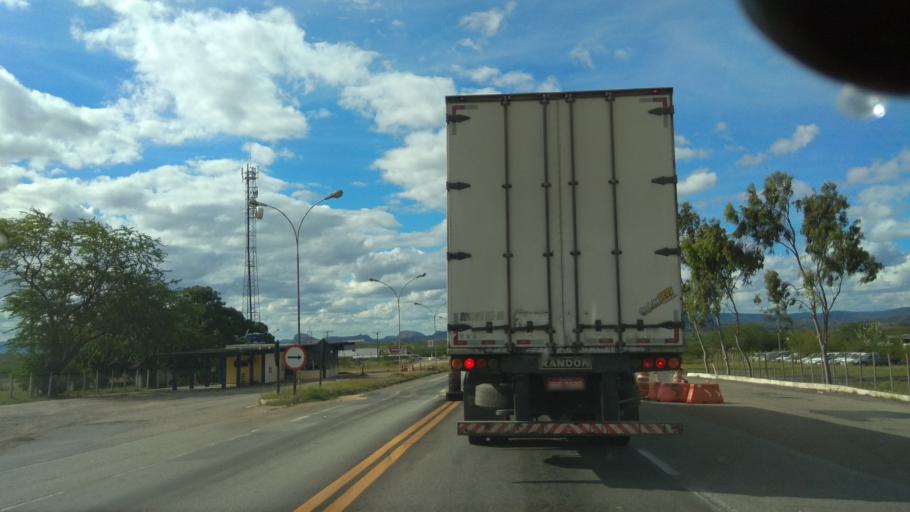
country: BR
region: Bahia
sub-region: Amargosa
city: Amargosa
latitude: -12.8568
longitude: -39.8482
